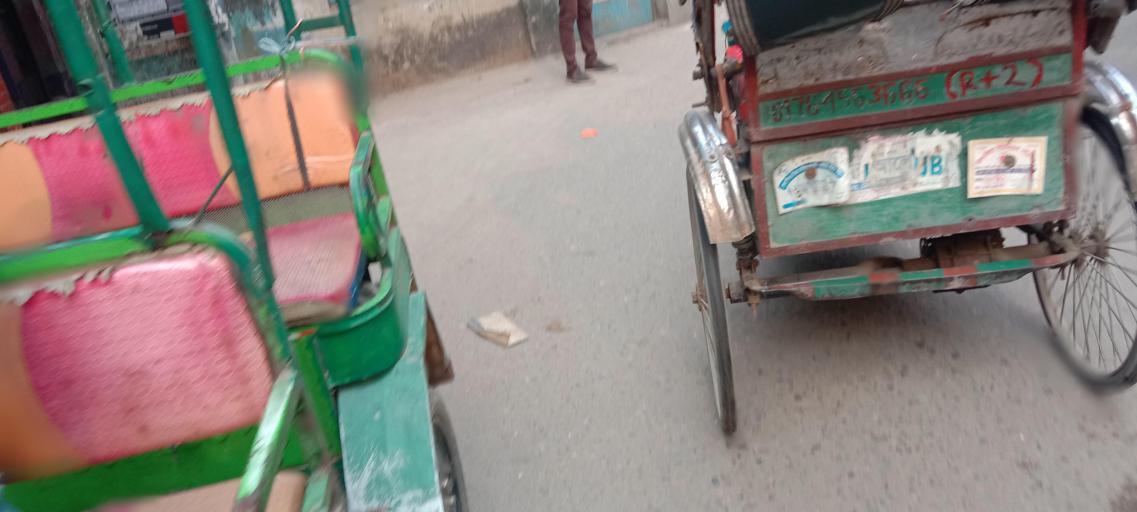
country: BD
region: Dhaka
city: Azimpur
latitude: 23.7057
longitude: 90.3831
